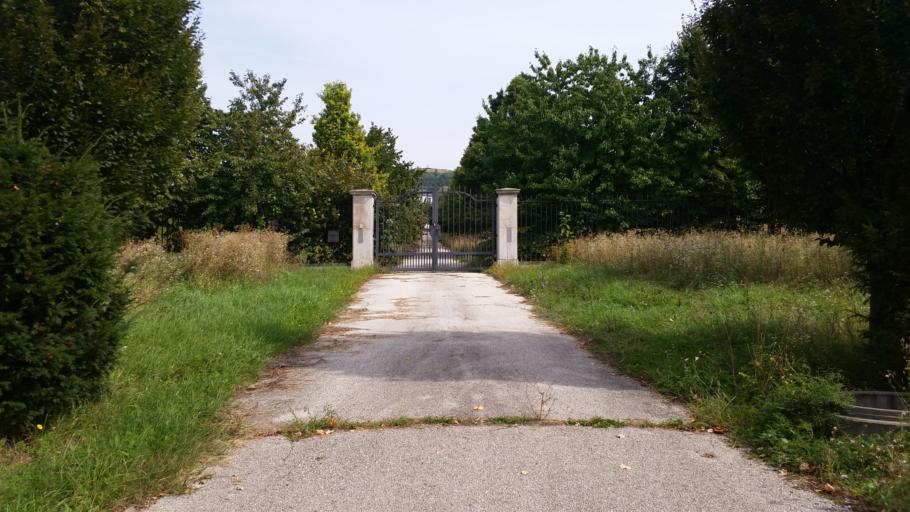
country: HU
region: Pest
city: Telki
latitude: 47.5659
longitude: 18.8124
